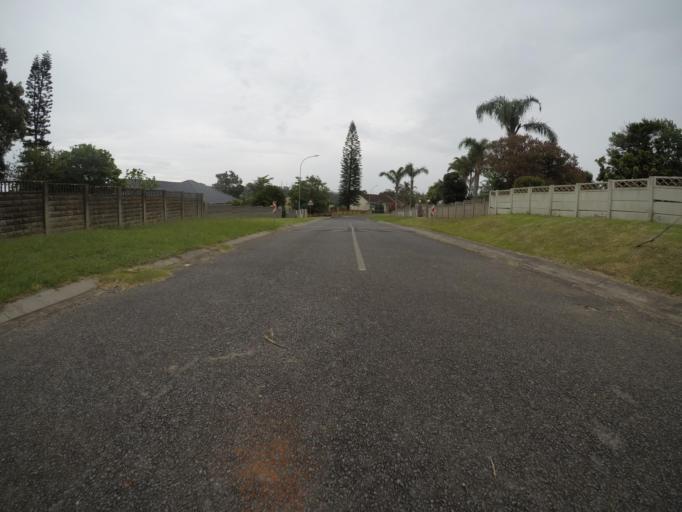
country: ZA
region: Eastern Cape
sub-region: Buffalo City Metropolitan Municipality
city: East London
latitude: -32.9888
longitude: 27.8565
